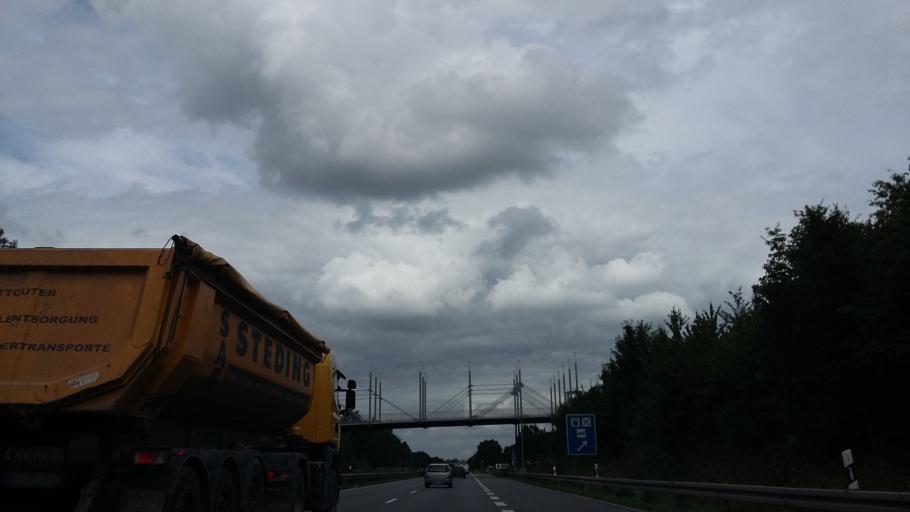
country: DE
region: Lower Saxony
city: Laatzen
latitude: 52.3204
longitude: 9.8134
